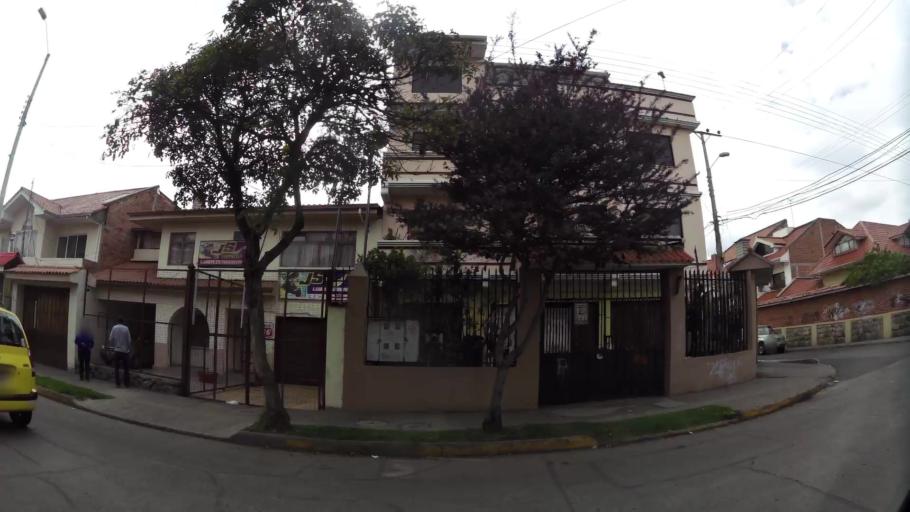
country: EC
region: Azuay
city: Cuenca
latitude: -2.8976
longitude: -78.9864
